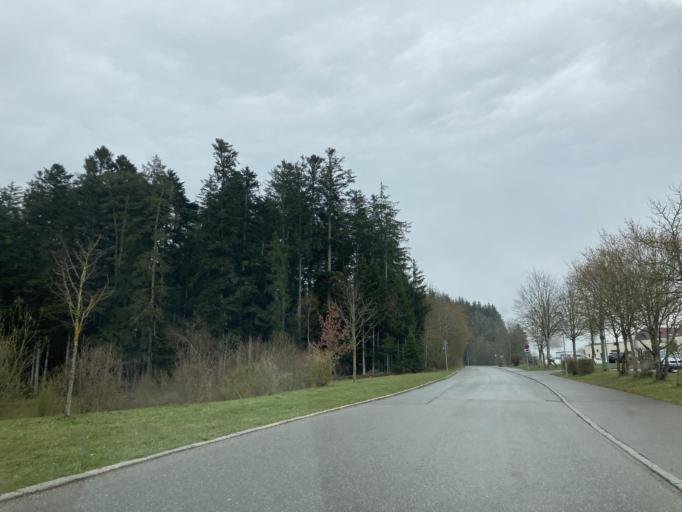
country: DE
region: Baden-Wuerttemberg
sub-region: Freiburg Region
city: Aichhalden
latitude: 48.2410
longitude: 8.4249
